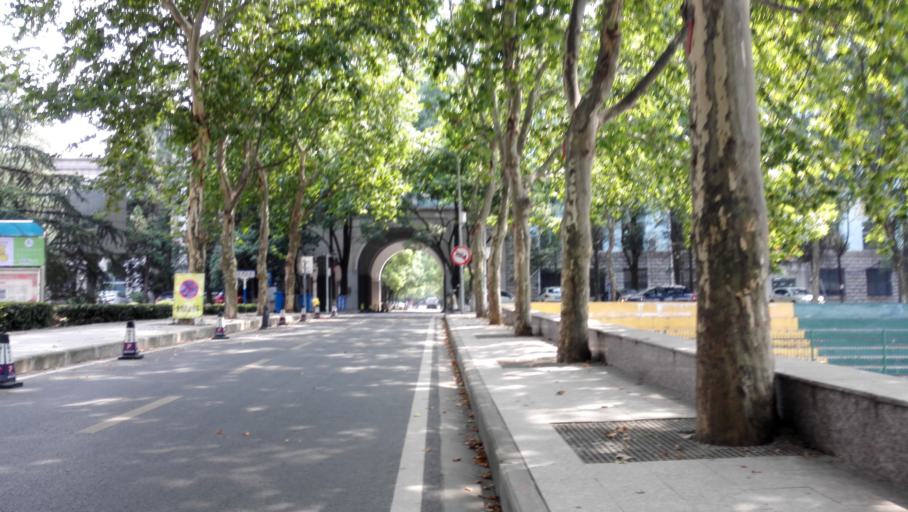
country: CN
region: Hubei
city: Shizishan
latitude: 30.5297
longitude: 114.3564
